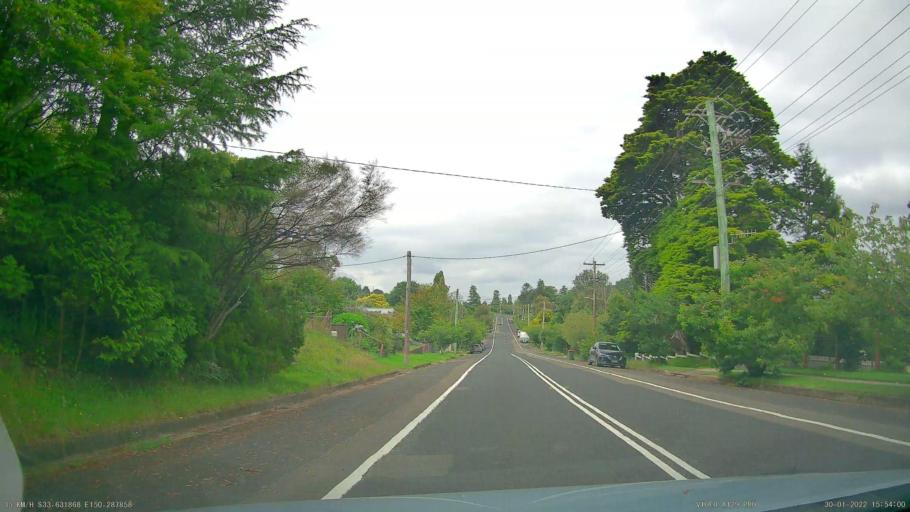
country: AU
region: New South Wales
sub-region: Blue Mountains Municipality
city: Blackheath
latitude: -33.6318
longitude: 150.2880
